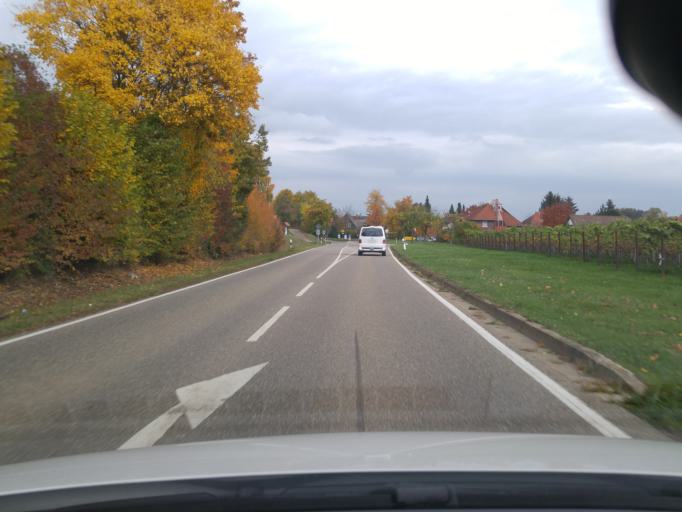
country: DE
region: Rheinland-Pfalz
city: Walsheim
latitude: 49.2374
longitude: 8.1184
